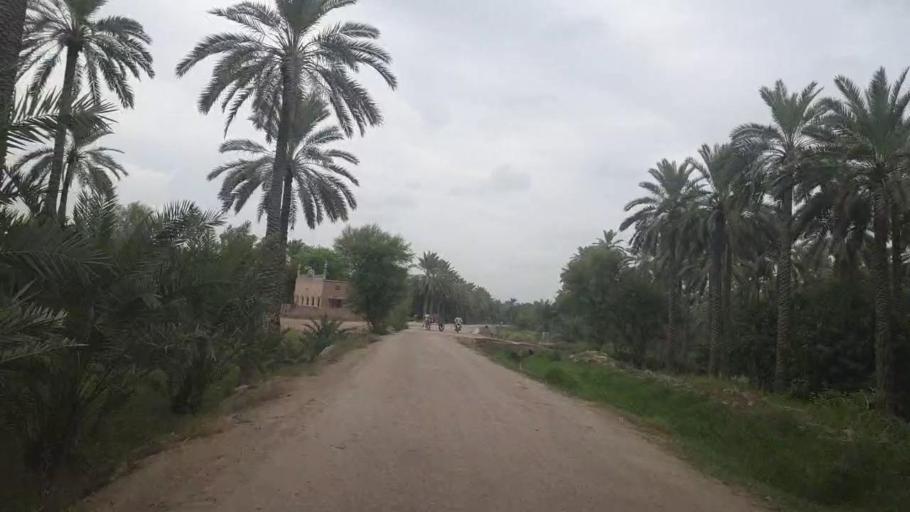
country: PK
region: Sindh
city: Khairpur
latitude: 27.5747
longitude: 68.7064
